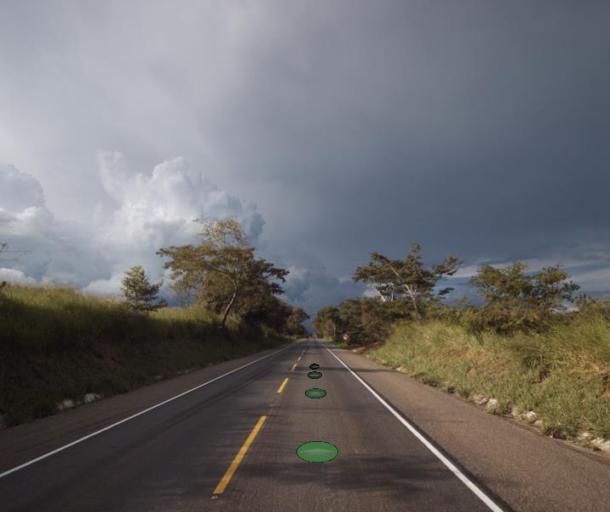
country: BR
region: Goias
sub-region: Ceres
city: Ceres
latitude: -15.1649
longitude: -49.5418
